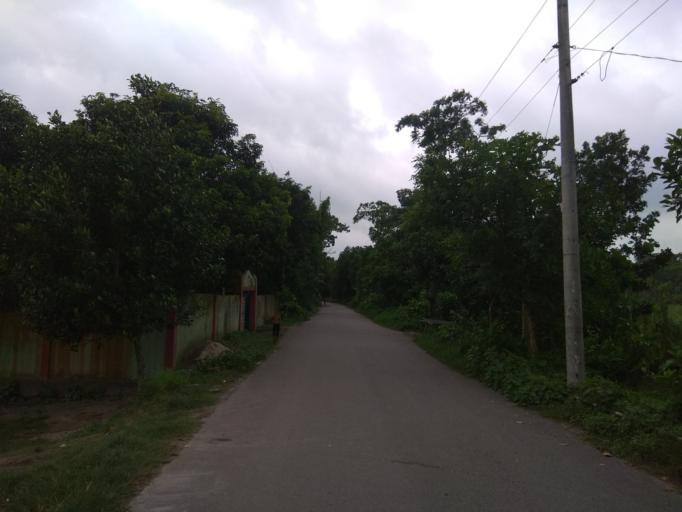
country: BD
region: Dhaka
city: Dohar
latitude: 23.4485
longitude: 90.0616
